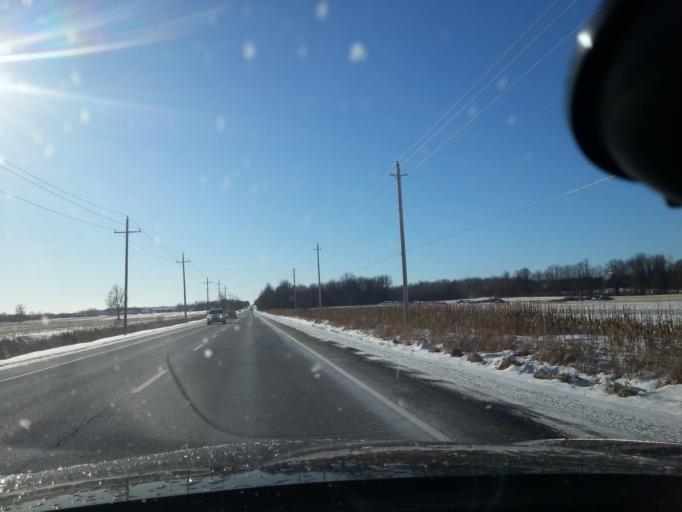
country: CA
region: Ontario
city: Ottawa
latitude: 45.2946
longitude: -75.5351
